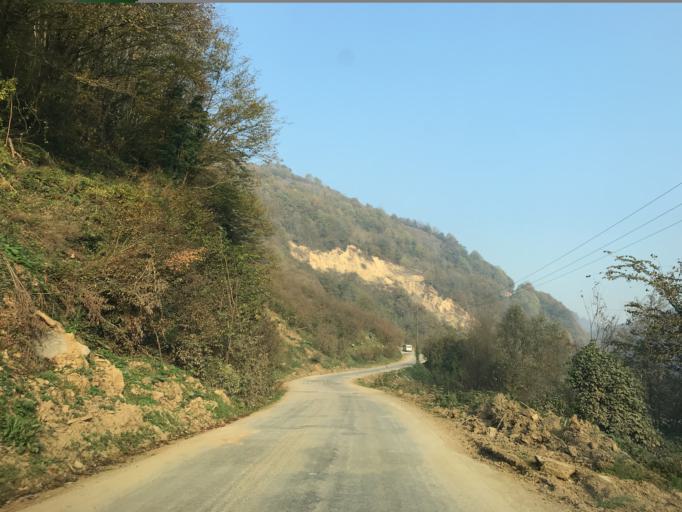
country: TR
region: Duzce
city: Cumayeri
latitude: 40.9196
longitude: 30.9296
